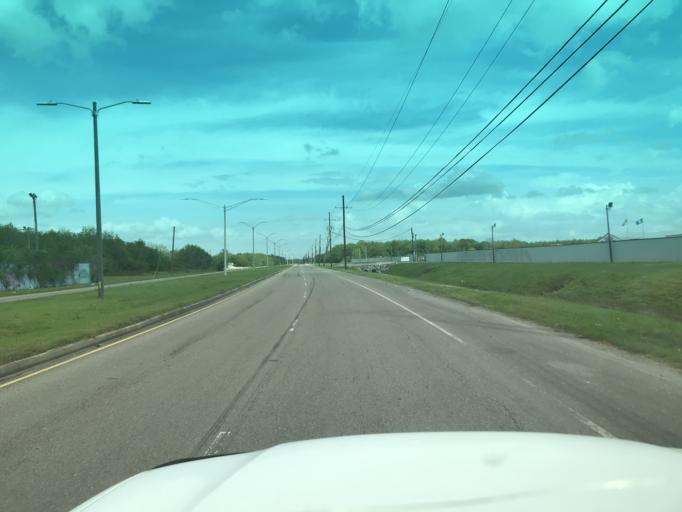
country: US
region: Louisiana
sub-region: Saint Bernard Parish
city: Arabi
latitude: 30.0041
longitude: -90.0130
